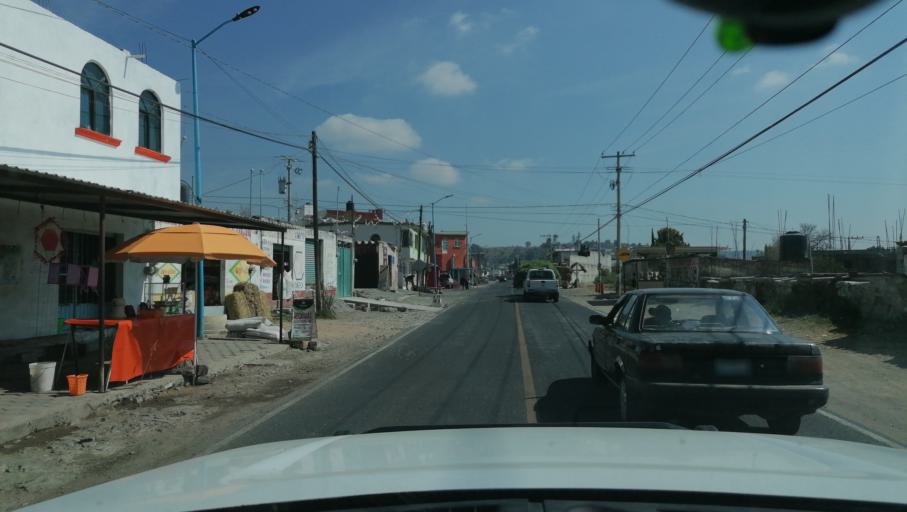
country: MX
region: Tlaxcala
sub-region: Tetlatlahuca
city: Santa Cruz Aquiahuac
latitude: 19.2342
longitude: -98.2852
